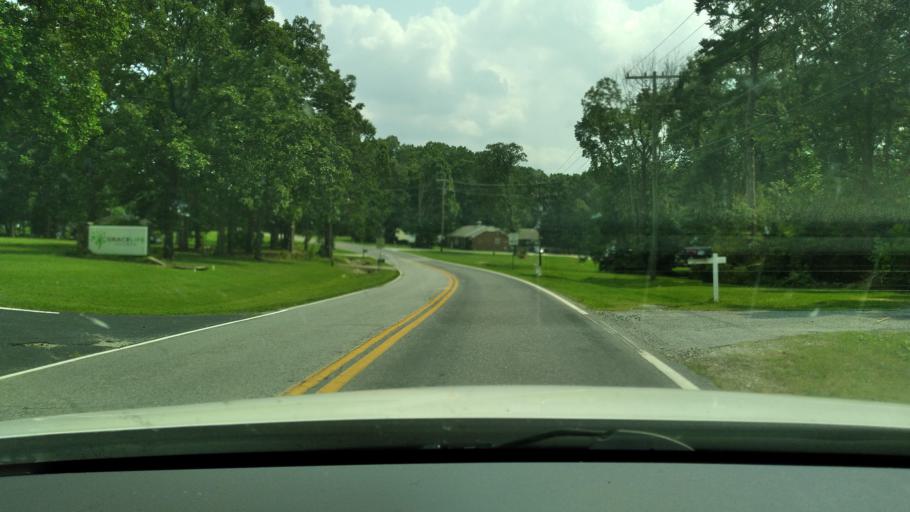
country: US
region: North Carolina
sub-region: Guilford County
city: Jamestown
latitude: 36.0424
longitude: -79.8908
